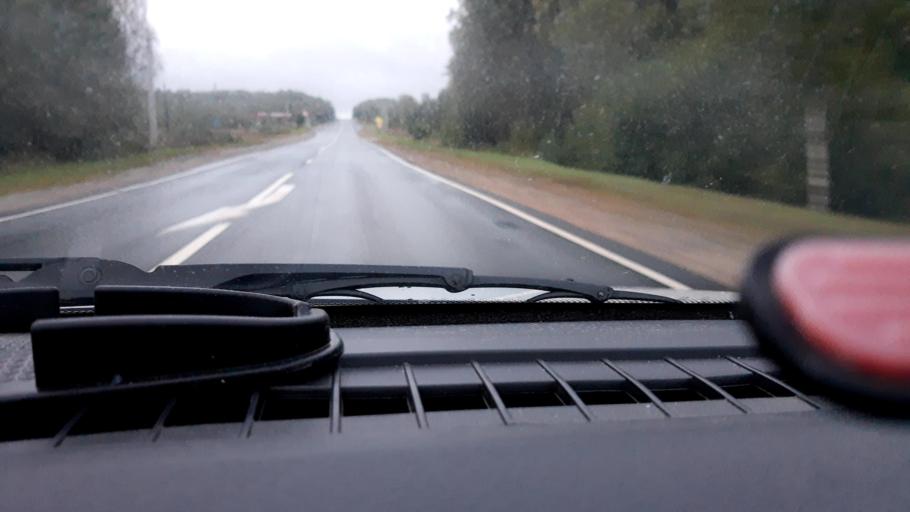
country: RU
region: Nizjnij Novgorod
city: Vladimirskoye
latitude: 56.9753
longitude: 45.1134
